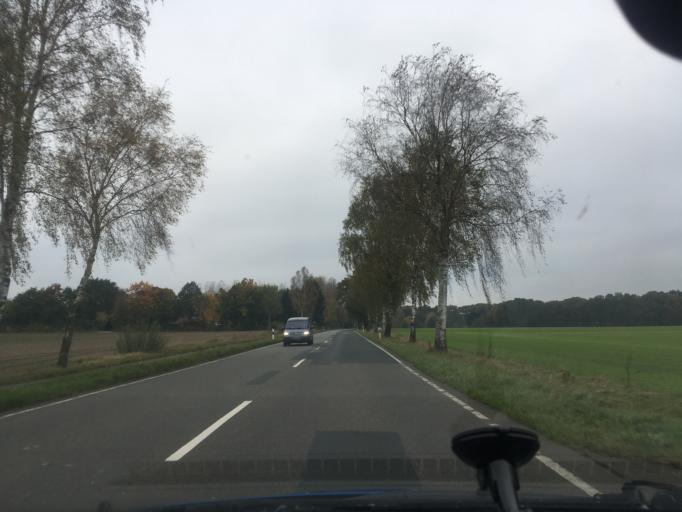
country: DE
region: Lower Saxony
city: Bispingen
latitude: 53.0221
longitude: 9.9991
